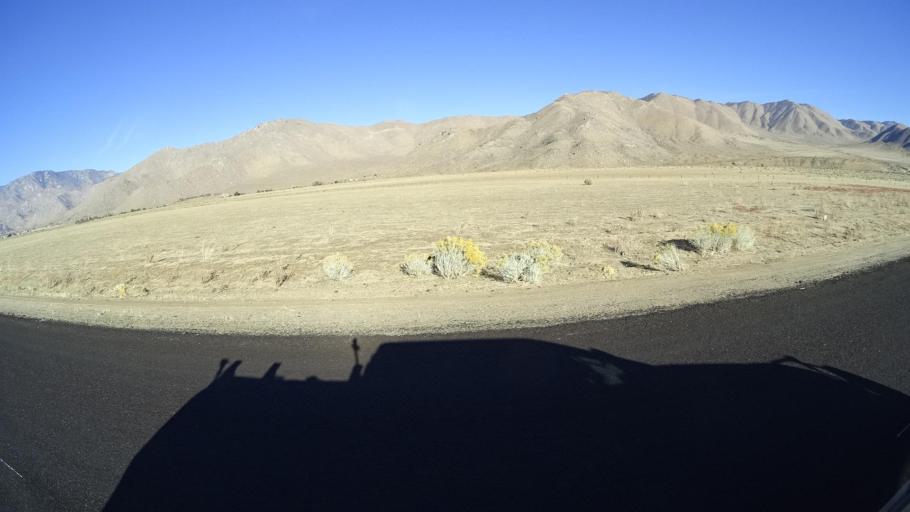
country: US
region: California
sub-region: Kern County
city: Weldon
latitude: 35.6200
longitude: -118.2565
